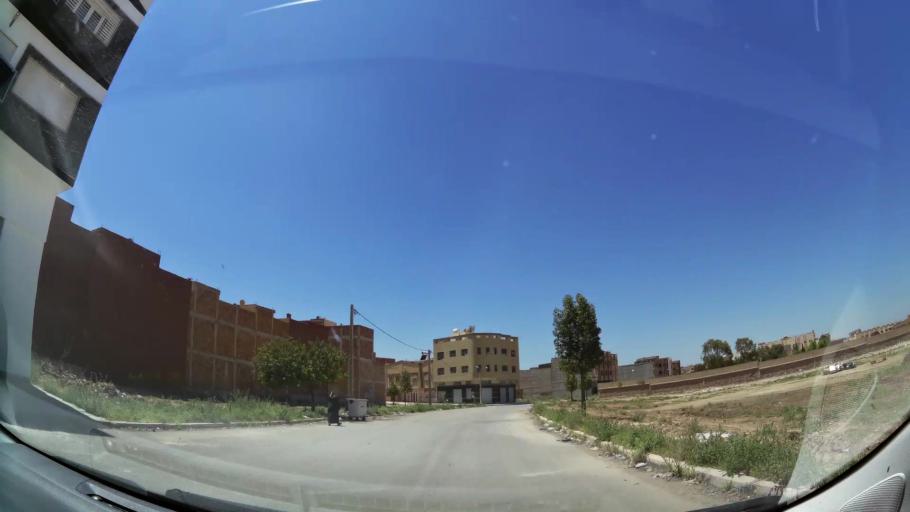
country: MA
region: Oriental
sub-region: Oujda-Angad
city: Oujda
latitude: 34.6685
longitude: -1.8793
